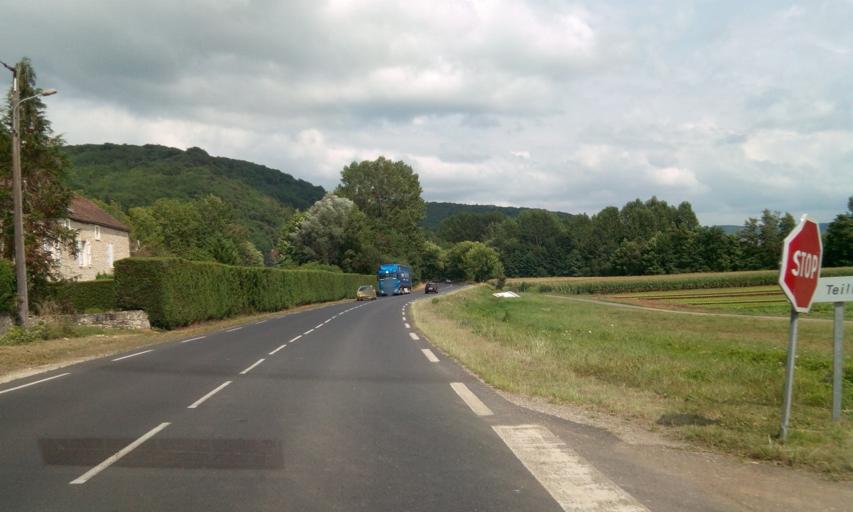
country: FR
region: Aquitaine
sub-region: Departement de la Dordogne
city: Eyvigues-et-Eybenes
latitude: 44.8885
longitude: 1.3930
